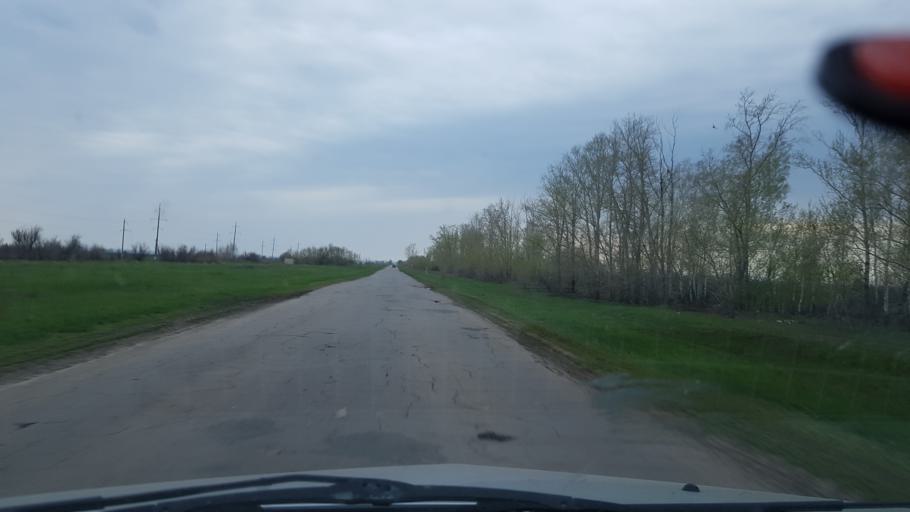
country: RU
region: Samara
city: Khryashchevka
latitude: 53.6681
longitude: 49.1420
